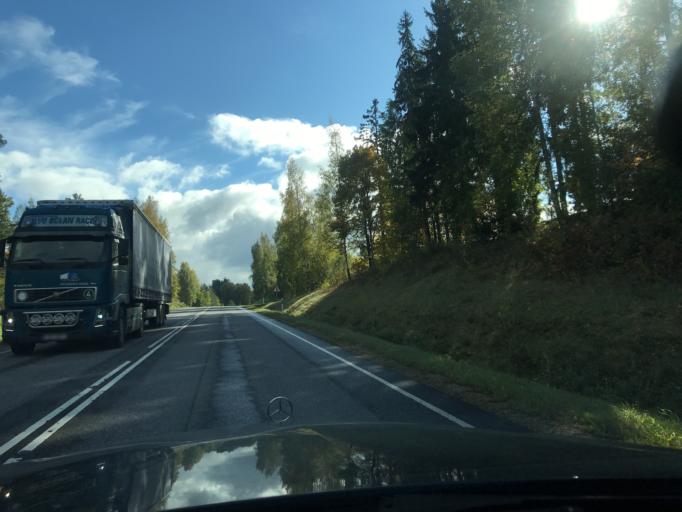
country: EE
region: Vorumaa
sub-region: Voru linn
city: Voru
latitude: 57.8009
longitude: 27.0884
